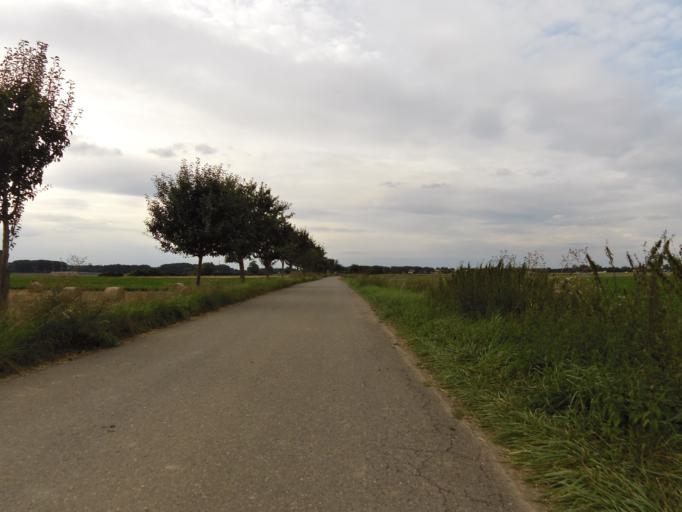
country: DE
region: Rheinland-Pfalz
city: Worms
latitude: 49.6234
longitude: 8.4056
